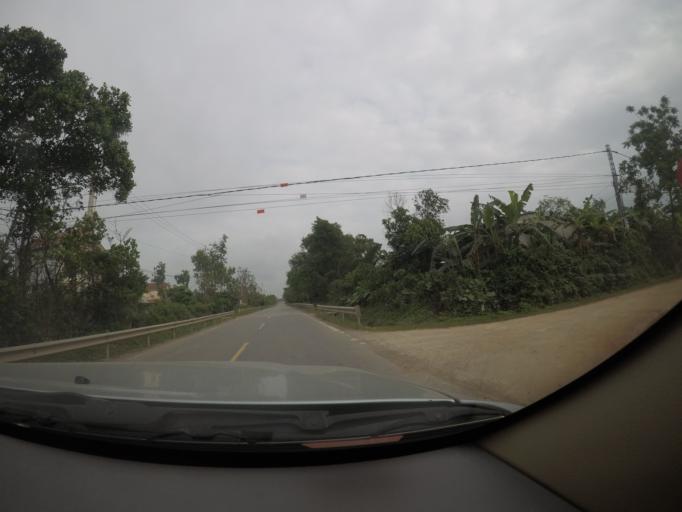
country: VN
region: Quang Binh
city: Kwang Binh
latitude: 17.4277
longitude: 106.5893
